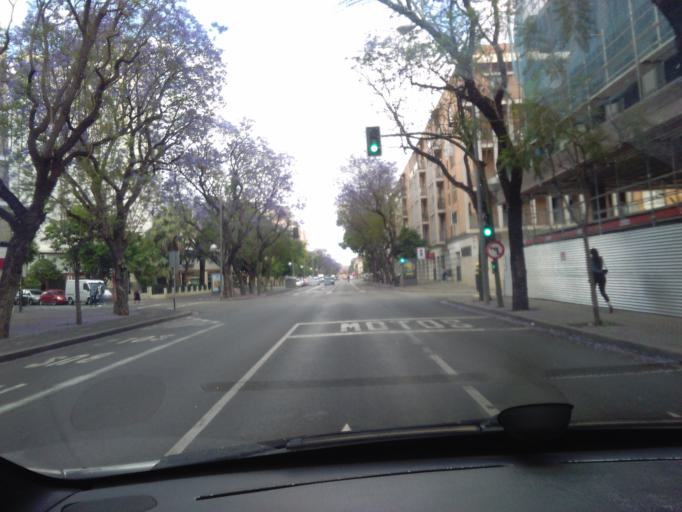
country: ES
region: Andalusia
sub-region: Provincia de Sevilla
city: Sevilla
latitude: 37.3766
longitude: -5.9736
